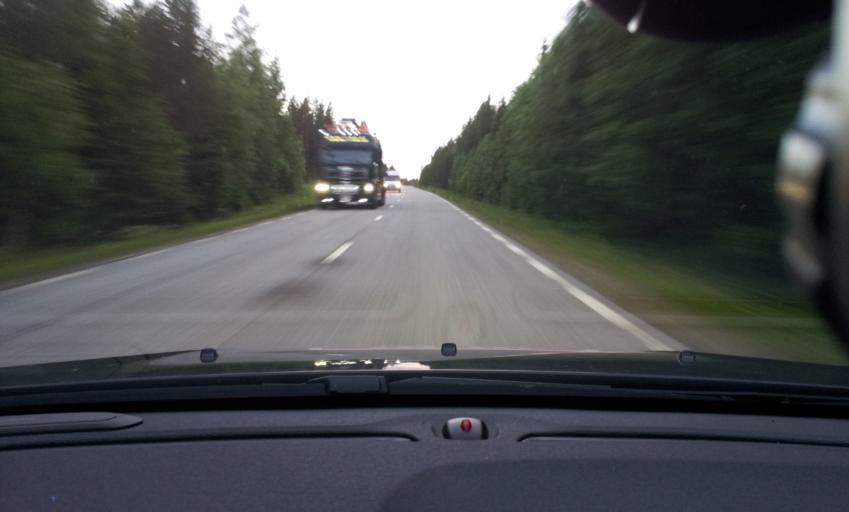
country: SE
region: Jaemtland
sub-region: Ragunda Kommun
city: Hammarstrand
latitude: 63.0292
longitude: 16.3271
